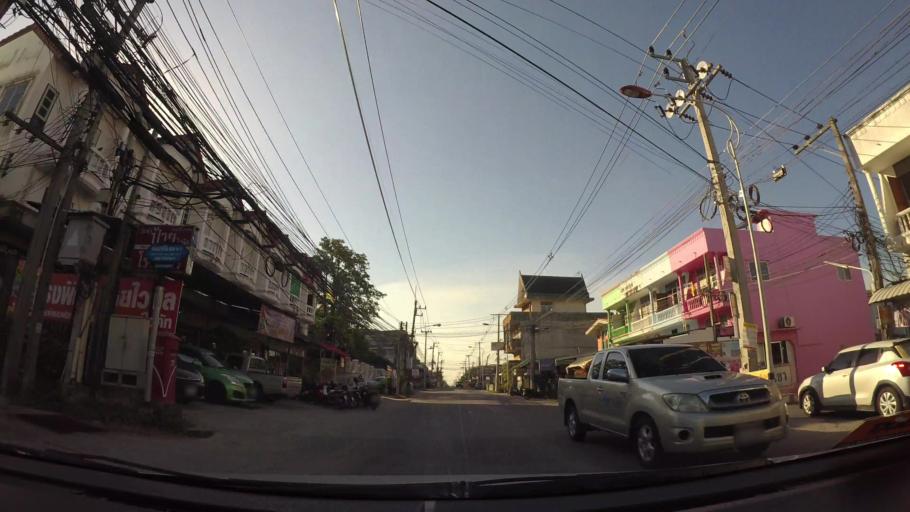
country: TH
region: Chon Buri
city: Si Racha
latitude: 13.1524
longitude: 100.9337
